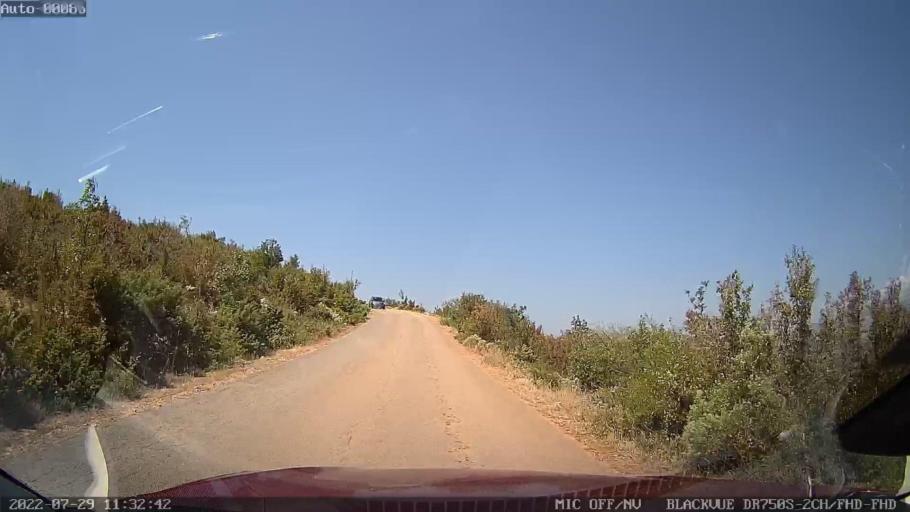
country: HR
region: Zadarska
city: Obrovac
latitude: 44.1909
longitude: 15.7353
